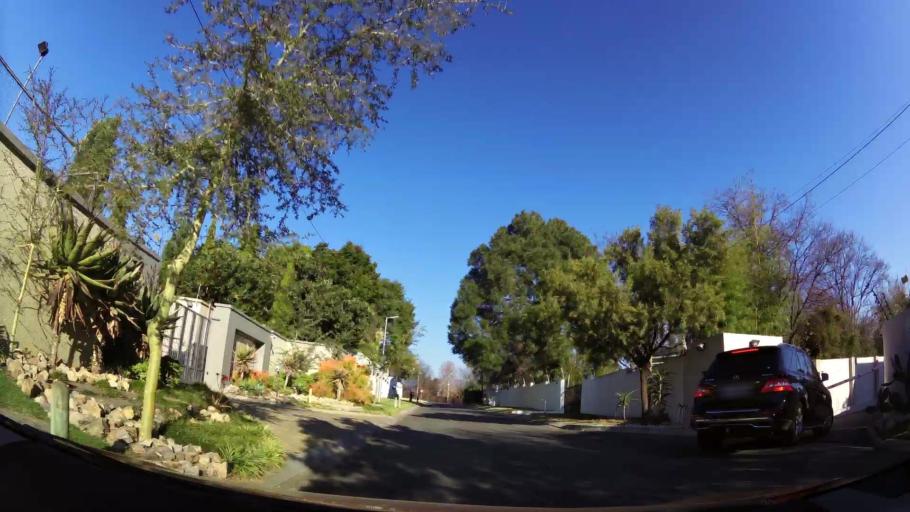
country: ZA
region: Gauteng
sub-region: City of Johannesburg Metropolitan Municipality
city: Midrand
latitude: -26.0710
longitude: 28.0597
